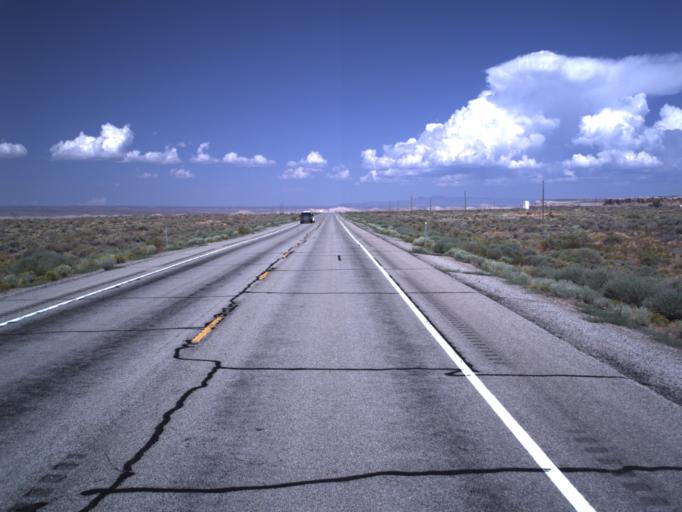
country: US
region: Utah
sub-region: San Juan County
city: Blanding
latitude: 37.1773
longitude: -109.5854
